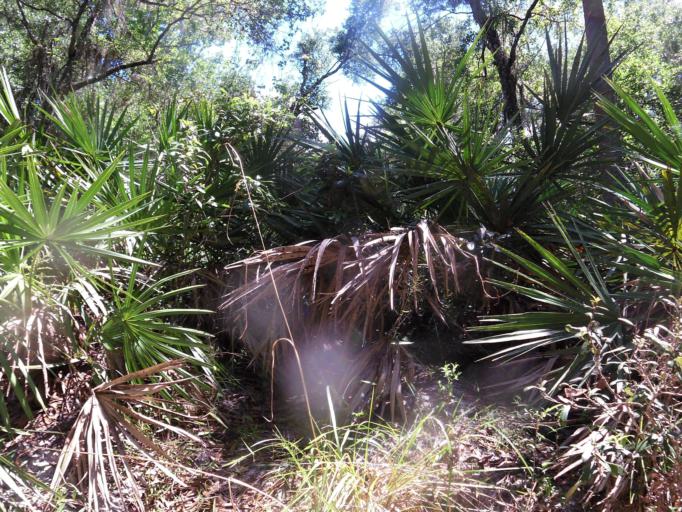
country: US
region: Florida
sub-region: Flagler County
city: Flagler Beach
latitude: 29.4111
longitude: -81.1281
